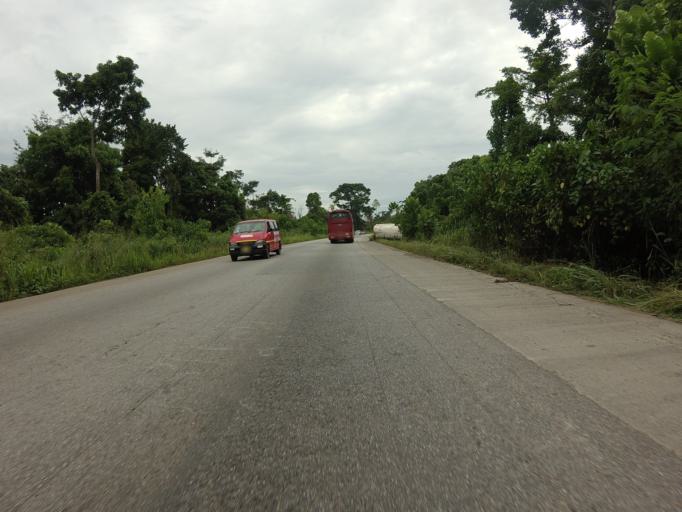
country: GH
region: Eastern
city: Nkawkaw
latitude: 6.6006
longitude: -0.9750
